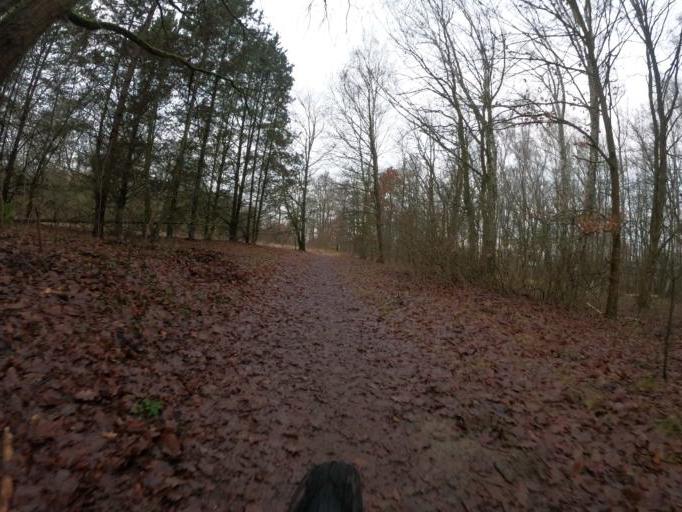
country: DE
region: Brandenburg
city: Schulzendorf
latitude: 52.3659
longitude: 13.5948
